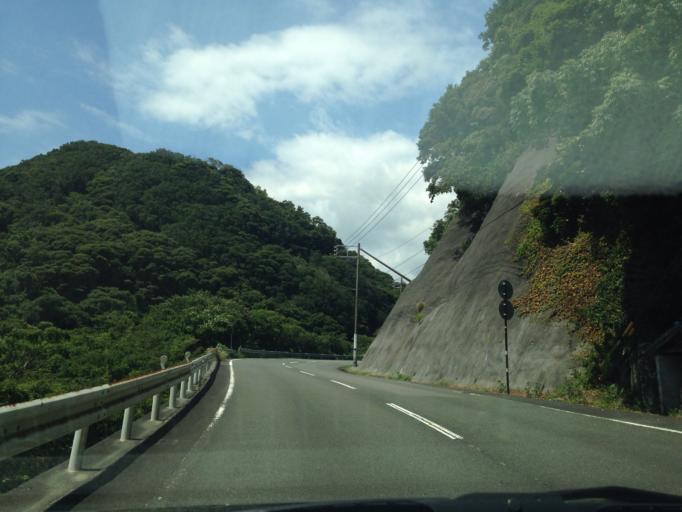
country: JP
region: Shizuoka
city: Shimoda
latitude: 34.6251
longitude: 138.8235
